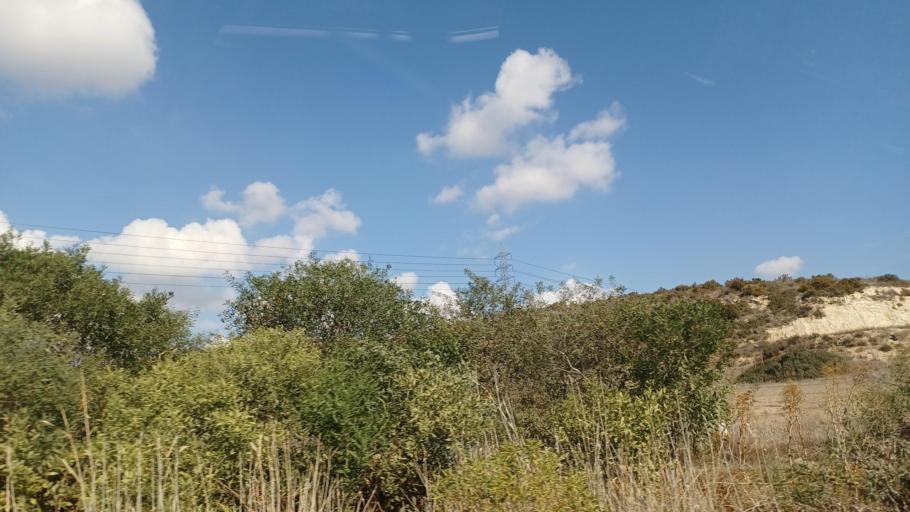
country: CY
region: Limassol
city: Pyrgos
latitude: 34.7234
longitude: 33.2545
